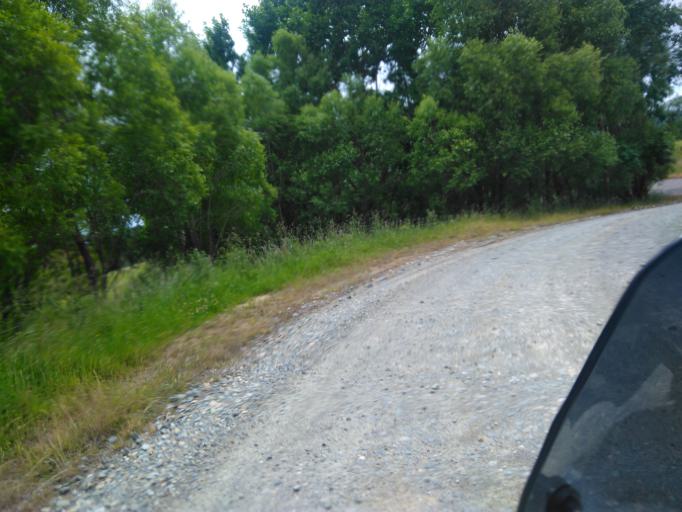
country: NZ
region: Gisborne
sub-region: Gisborne District
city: Gisborne
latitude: -38.1889
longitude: 178.1008
